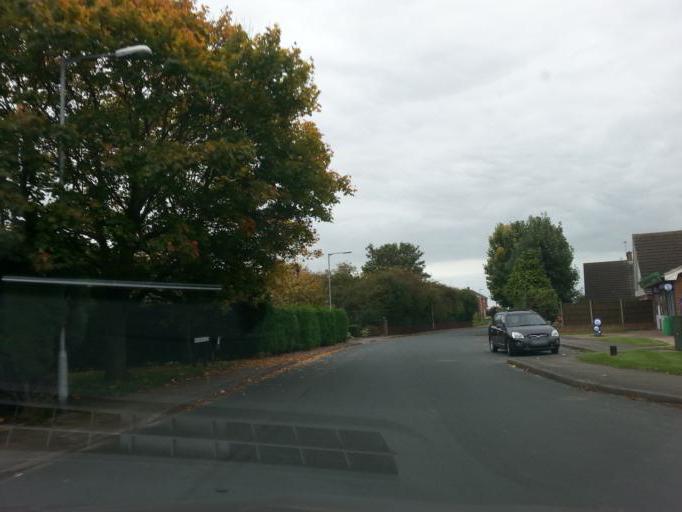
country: GB
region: England
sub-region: Nottinghamshire
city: Newark on Trent
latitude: 53.0745
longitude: -0.7794
